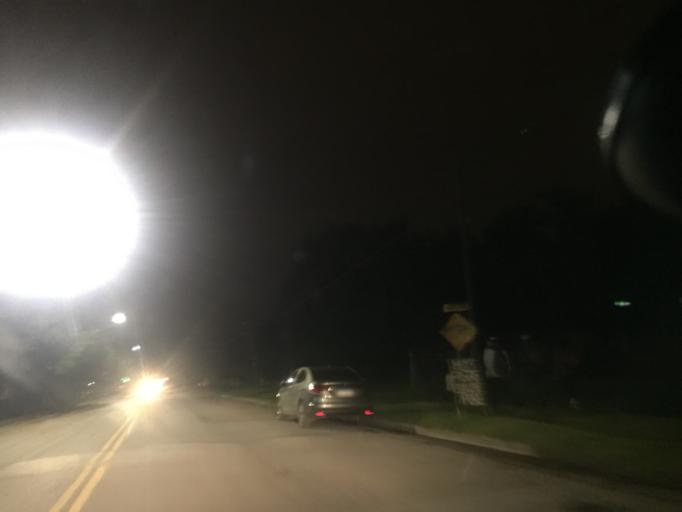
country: AR
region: Cordoba
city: Villa Allende
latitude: -31.3017
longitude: -64.2882
